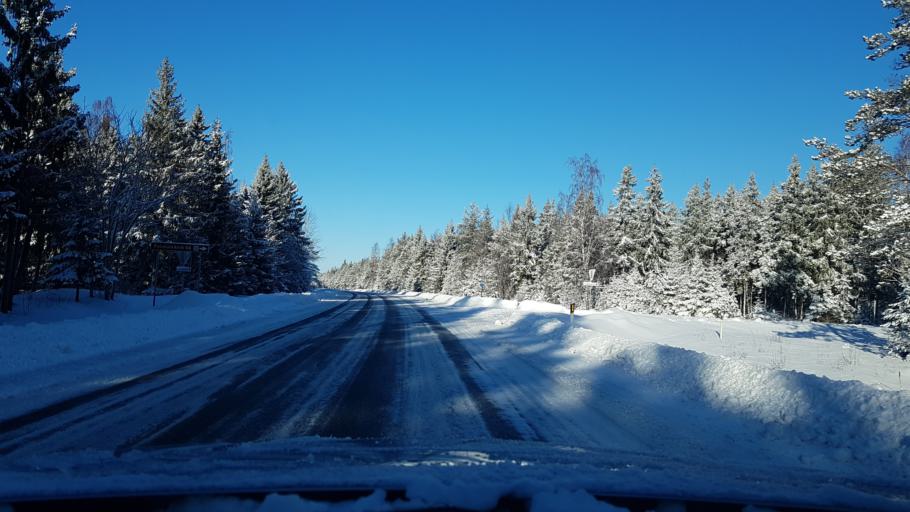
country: EE
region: Hiiumaa
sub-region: Kaerdla linn
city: Kardla
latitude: 58.9813
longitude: 22.8082
